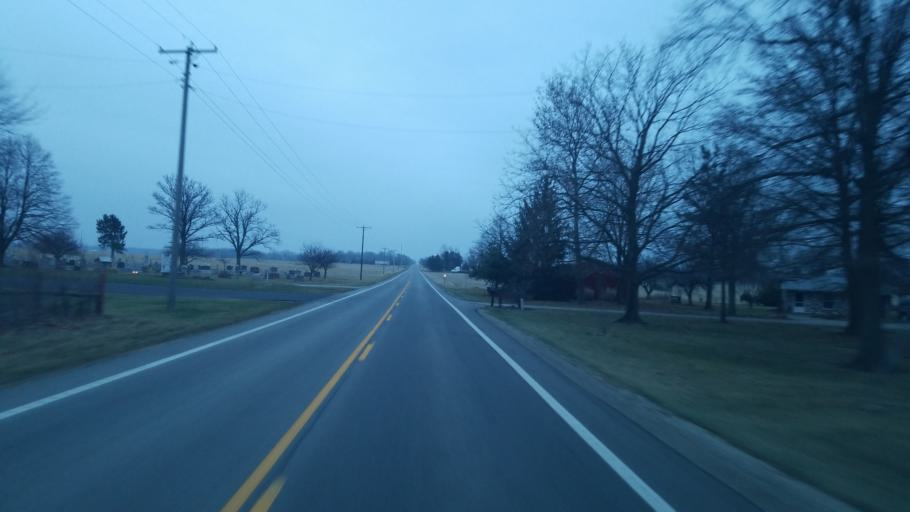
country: US
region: Ohio
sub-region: Mercer County
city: Rockford
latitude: 40.6550
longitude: -84.6410
